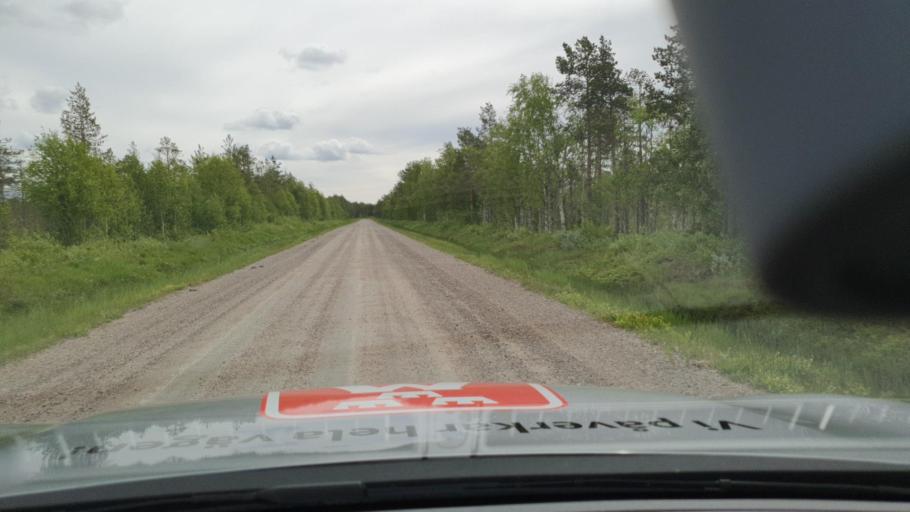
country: FI
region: Lapland
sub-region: Torniolaakso
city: Ylitornio
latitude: 65.9571
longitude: 23.7440
